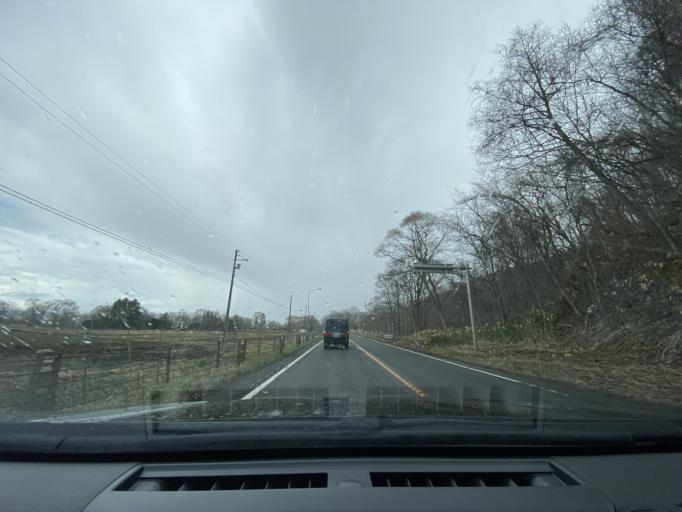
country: JP
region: Hokkaido
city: Fukagawa
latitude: 43.7045
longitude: 142.0939
